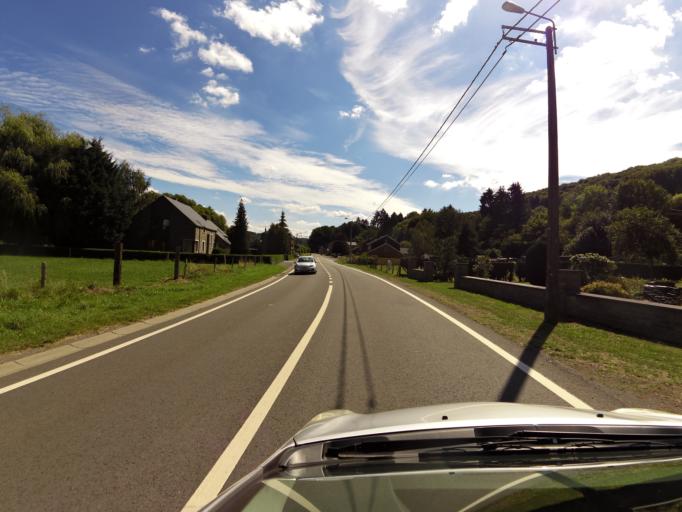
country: BE
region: Wallonia
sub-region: Province du Luxembourg
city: Hotton
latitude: 50.2555
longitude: 5.4766
